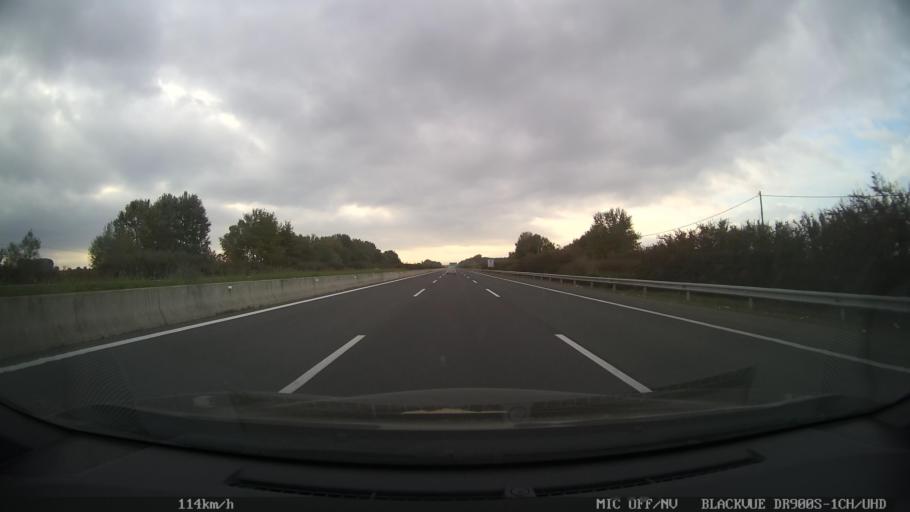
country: GR
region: Central Macedonia
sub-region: Nomos Pierias
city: Nea Efesos
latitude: 40.2136
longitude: 22.5434
